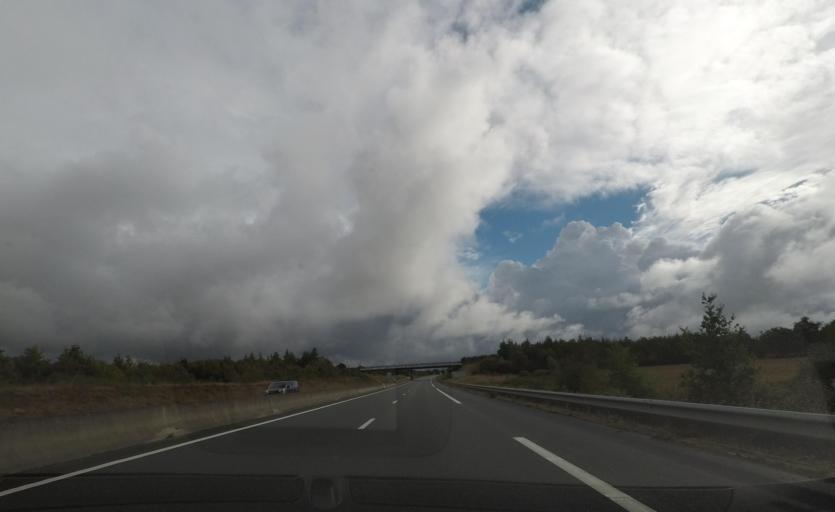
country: FR
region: Pays de la Loire
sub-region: Departement de la Vendee
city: La Roche-sur-Yon
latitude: 46.6514
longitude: -1.3863
